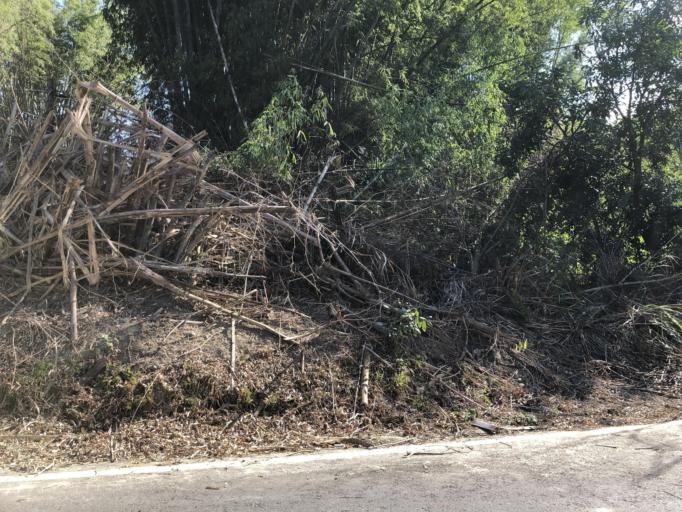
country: TW
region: Taiwan
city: Yujing
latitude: 23.0283
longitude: 120.3940
